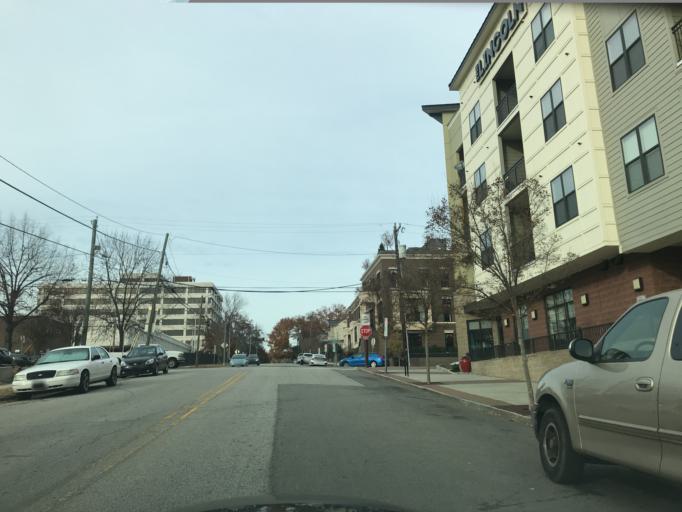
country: US
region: North Carolina
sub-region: Wake County
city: Raleigh
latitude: 35.7777
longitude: -78.6333
